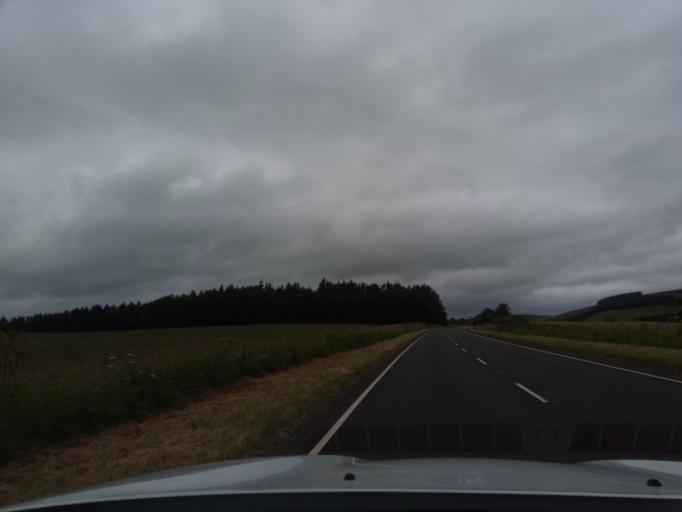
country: GB
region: Scotland
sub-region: The Scottish Borders
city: Lauder
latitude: 55.7607
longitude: -2.7805
